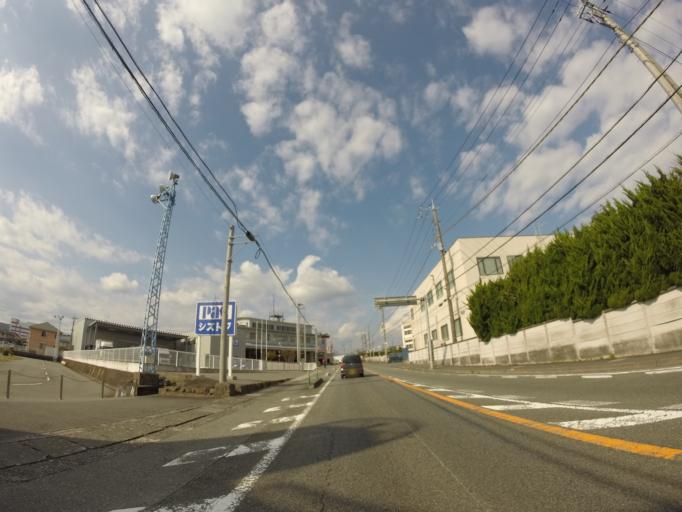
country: JP
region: Shizuoka
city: Fujinomiya
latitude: 35.2196
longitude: 138.6216
